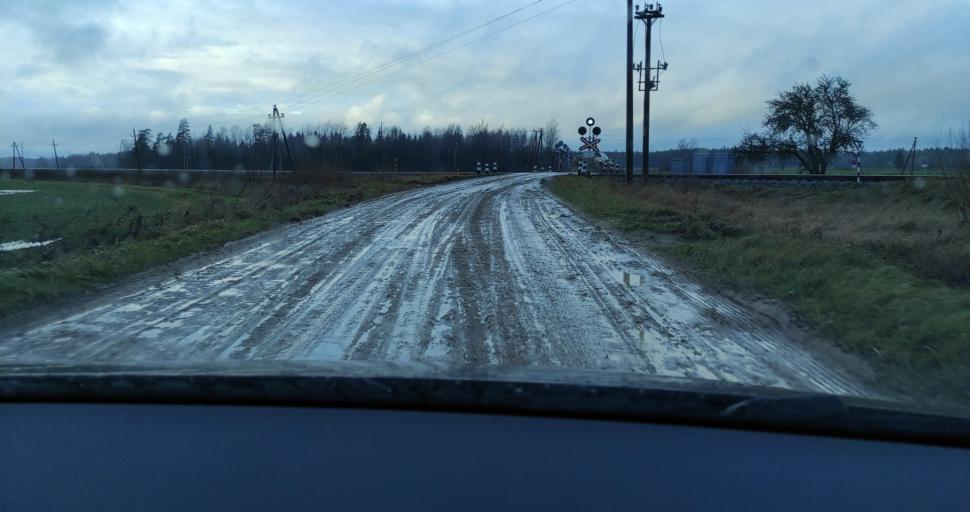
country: LV
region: Skrunda
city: Skrunda
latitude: 56.7106
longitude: 22.2016
